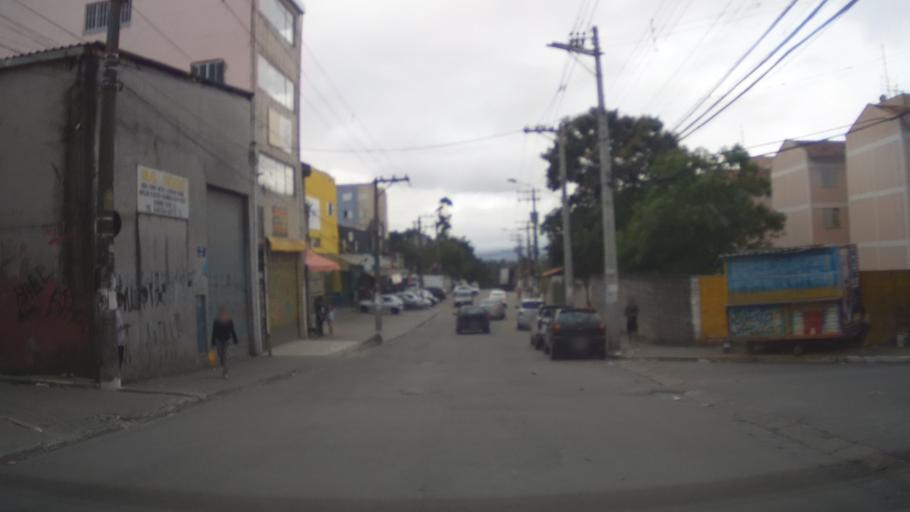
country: BR
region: Sao Paulo
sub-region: Itaquaquecetuba
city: Itaquaquecetuba
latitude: -23.4523
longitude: -46.4001
